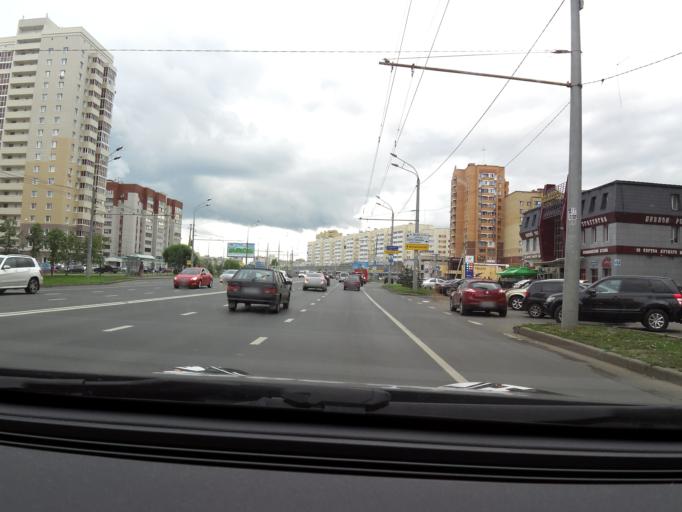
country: RU
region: Tatarstan
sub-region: Gorod Kazan'
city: Kazan
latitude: 55.8194
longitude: 49.1075
